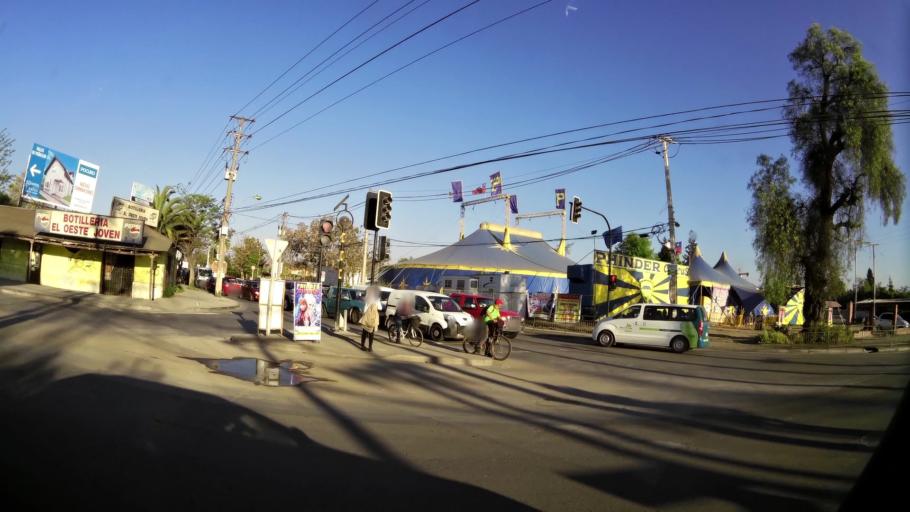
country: CL
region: Santiago Metropolitan
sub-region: Provincia de Talagante
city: Penaflor
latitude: -33.6097
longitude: -70.8574
